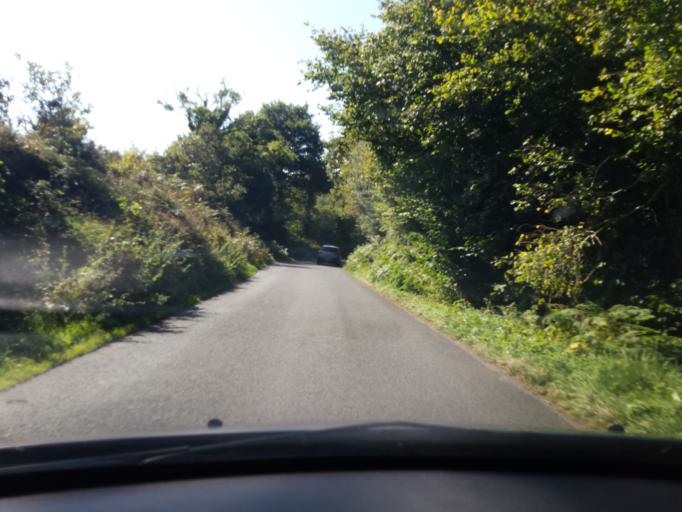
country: FR
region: Brittany
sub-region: Departement des Cotes-d'Armor
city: Plounevez-Quintin
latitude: 48.3432
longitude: -3.2438
